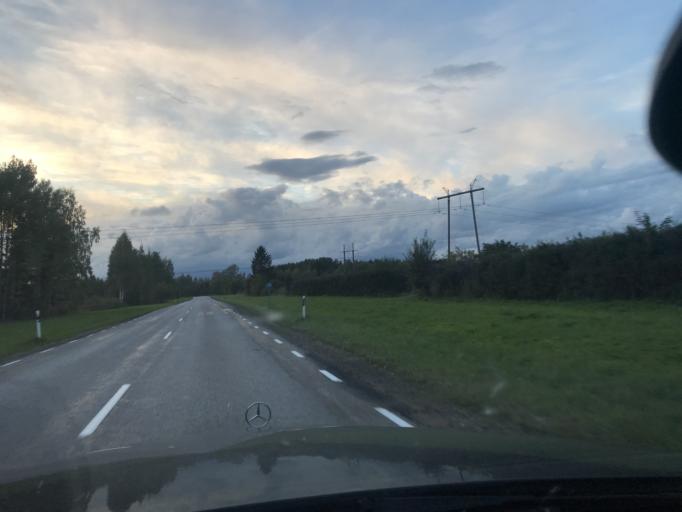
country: EE
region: Valgamaa
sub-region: Torva linn
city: Torva
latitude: 58.0115
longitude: 26.1807
